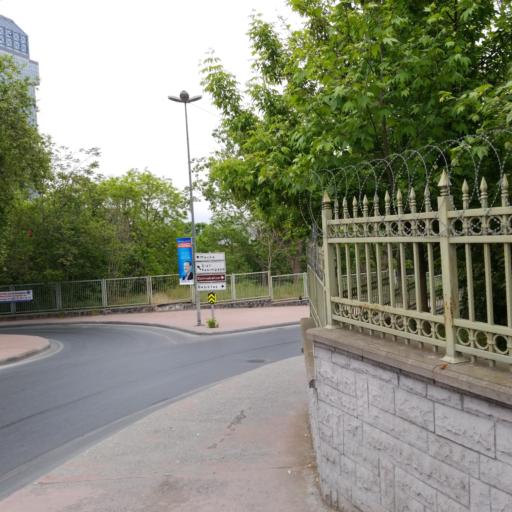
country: TR
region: Istanbul
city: Sisli
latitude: 41.0401
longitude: 28.9892
